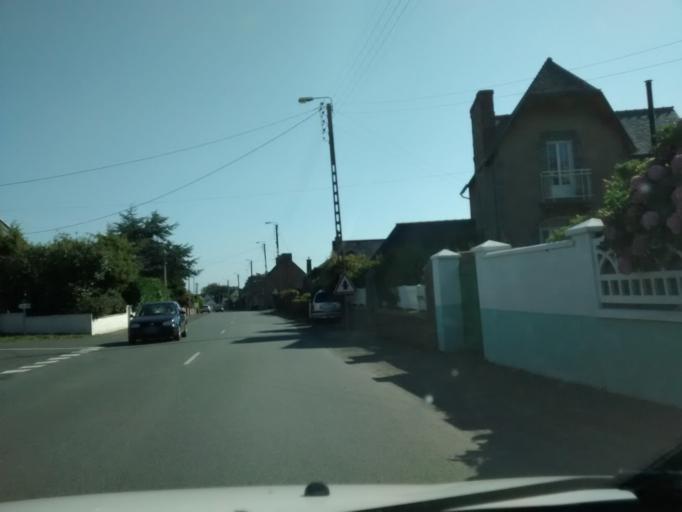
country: FR
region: Brittany
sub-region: Departement des Cotes-d'Armor
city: Pleubian
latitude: 48.8577
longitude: -3.1084
